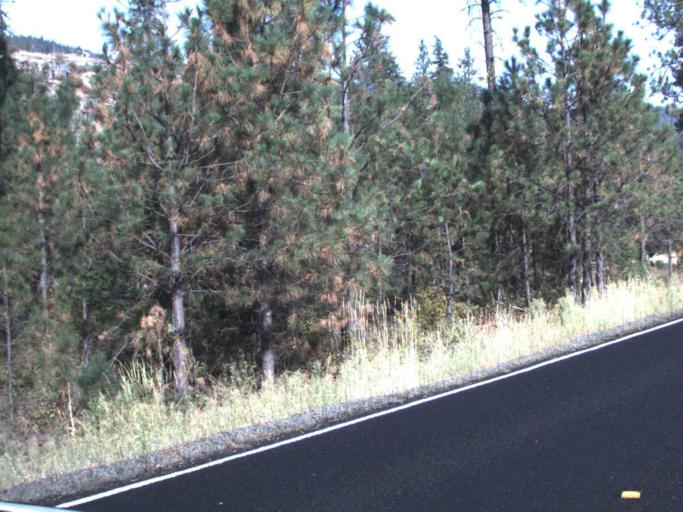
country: US
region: Washington
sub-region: Spokane County
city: Airway Heights
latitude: 47.8612
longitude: -117.7121
